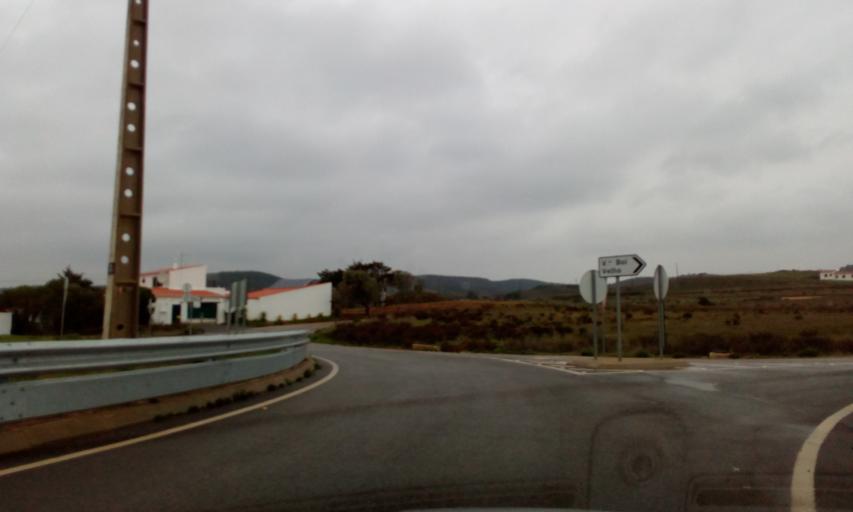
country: PT
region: Faro
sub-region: Vila do Bispo
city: Vila do Bispo
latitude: 37.0928
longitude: -8.8121
